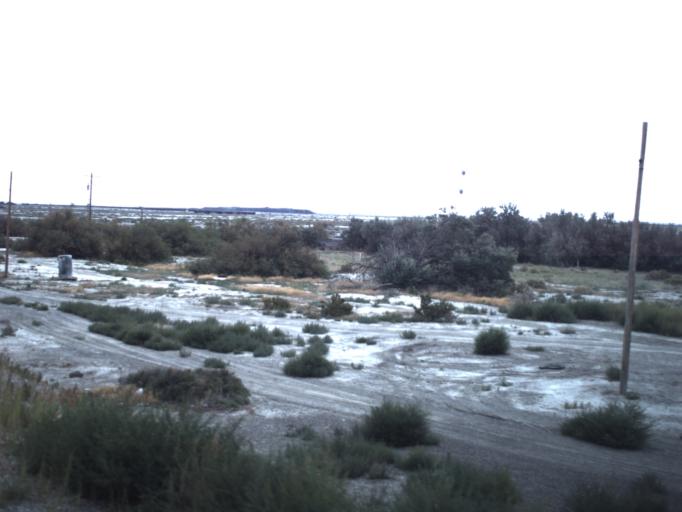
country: US
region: Utah
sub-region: Tooele County
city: Wendover
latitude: 40.7378
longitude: -114.0277
